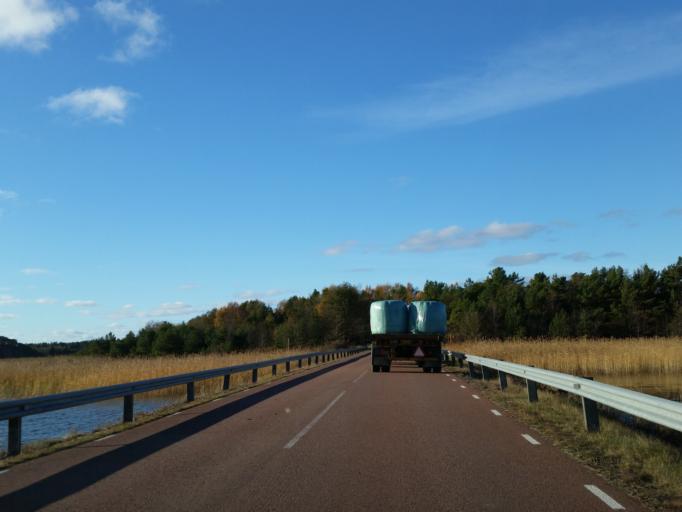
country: AX
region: Alands landsbygd
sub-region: Geta
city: Geta
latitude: 60.3660
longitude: 19.7772
